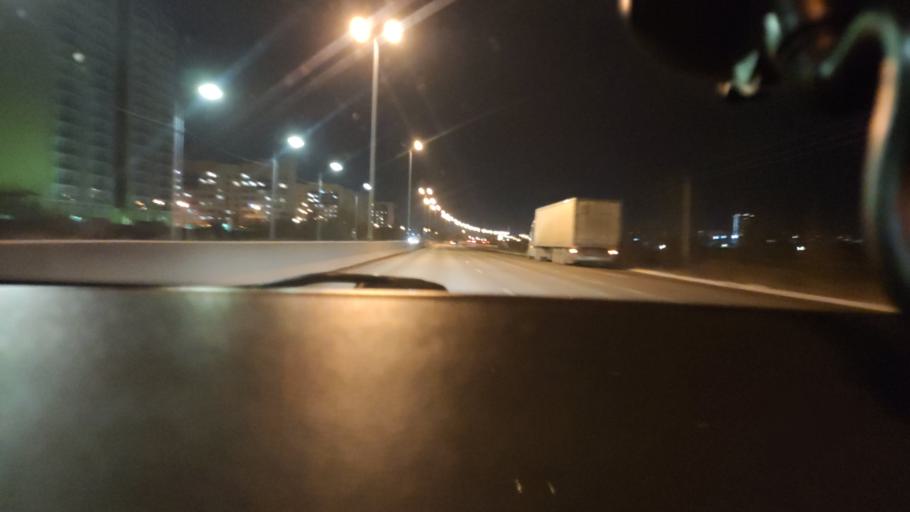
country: RU
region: Perm
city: Kondratovo
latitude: 57.9994
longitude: 56.1067
